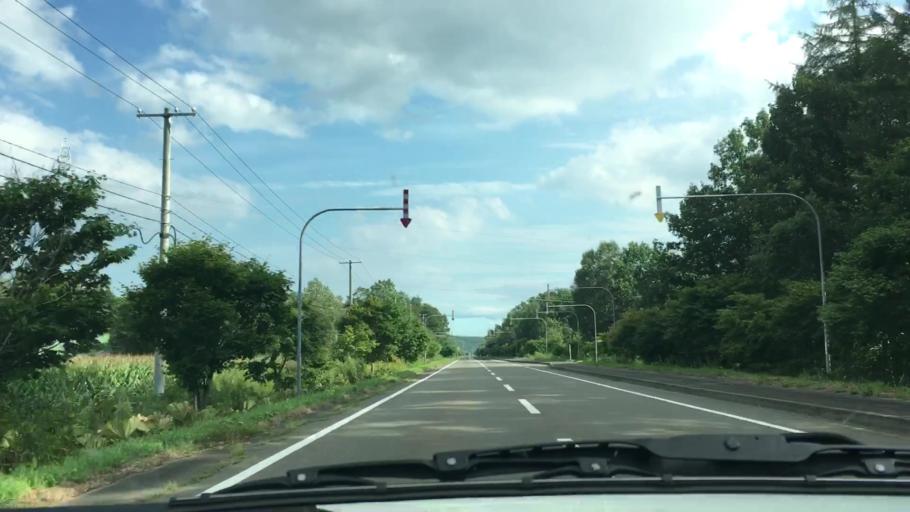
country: JP
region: Hokkaido
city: Otofuke
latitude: 43.3200
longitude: 143.3025
